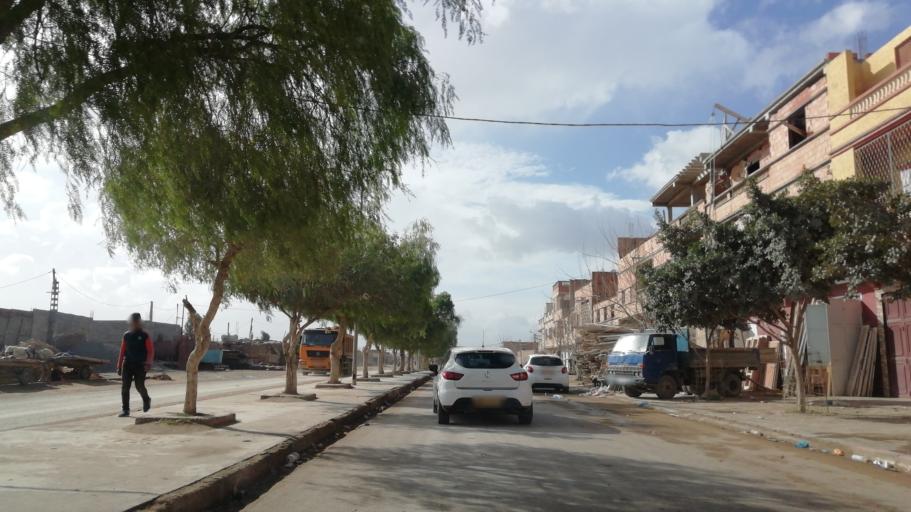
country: DZ
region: Oran
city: Es Senia
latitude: 35.6383
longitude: -0.5758
